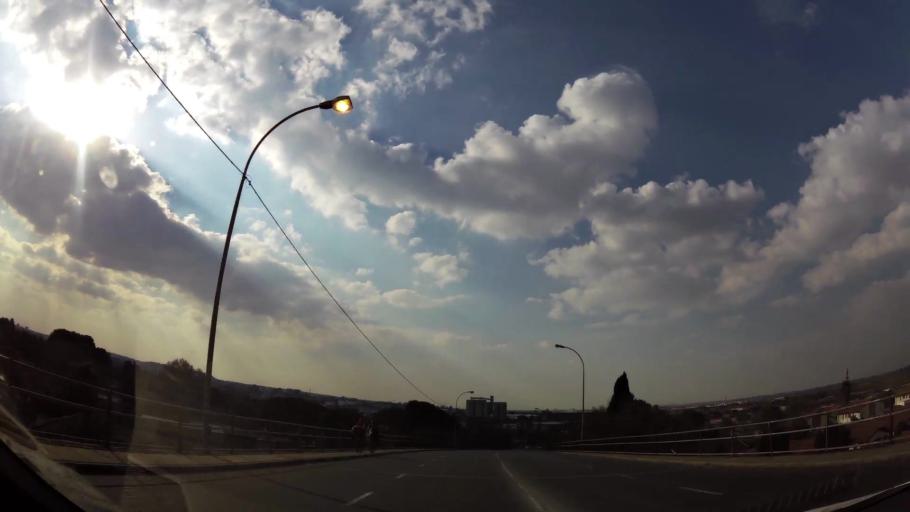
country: ZA
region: Gauteng
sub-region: Ekurhuleni Metropolitan Municipality
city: Germiston
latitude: -26.2350
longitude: 28.1855
